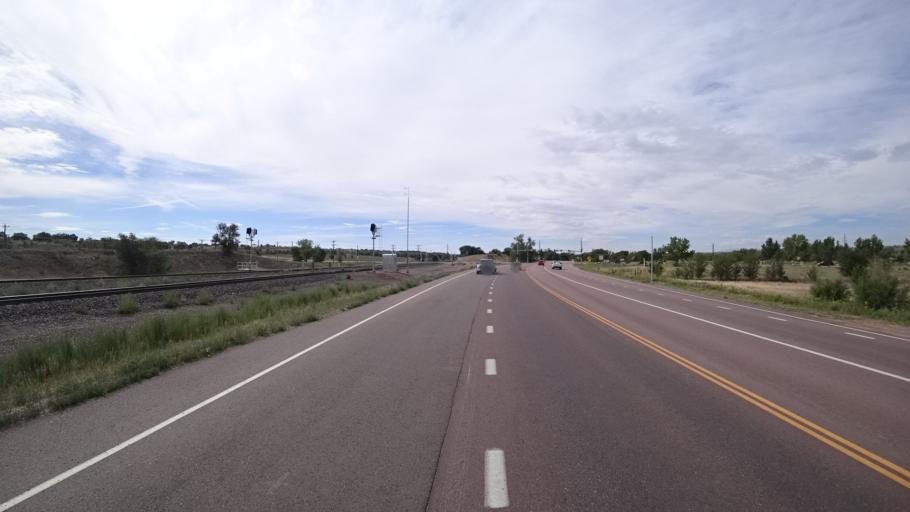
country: US
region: Colorado
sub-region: El Paso County
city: Fountain
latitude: 38.7107
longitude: -104.7120
